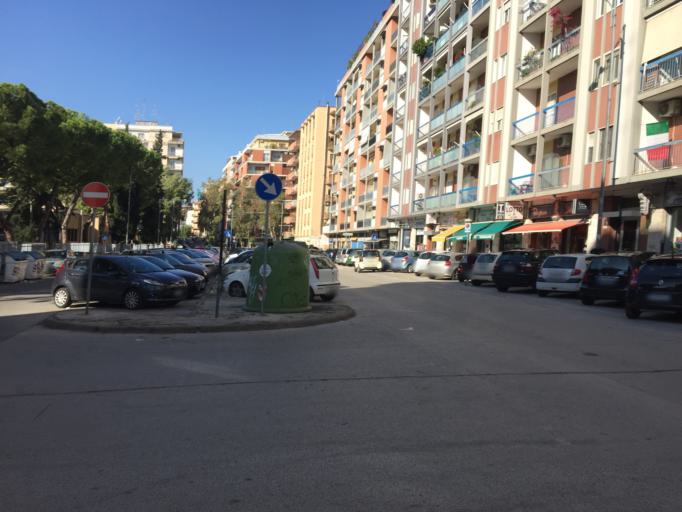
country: IT
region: Apulia
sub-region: Provincia di Bari
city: Bari
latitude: 41.1142
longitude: 16.8657
